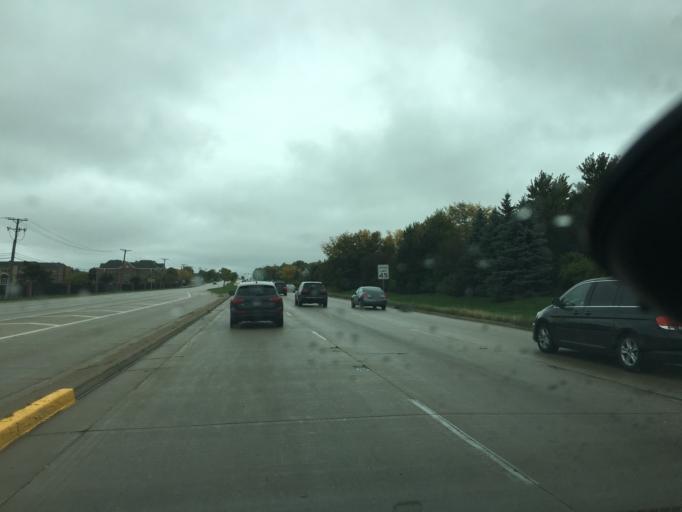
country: US
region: Illinois
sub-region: DuPage County
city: Naperville
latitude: 41.7270
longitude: -88.2061
